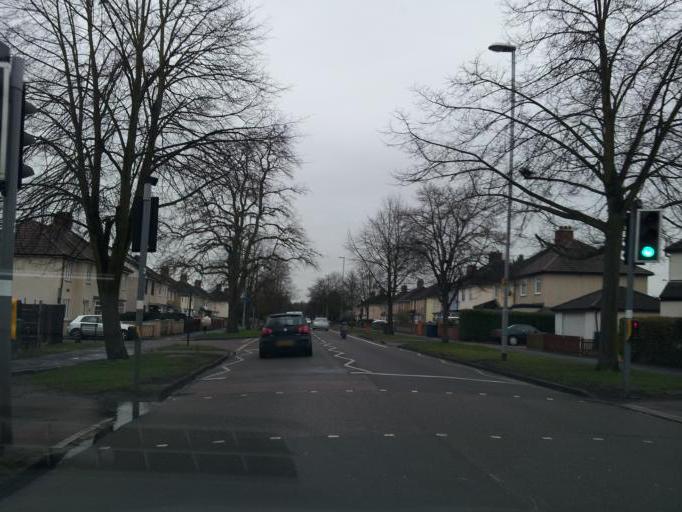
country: GB
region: England
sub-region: Cambridgeshire
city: Cambridge
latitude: 52.1826
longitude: 0.1506
